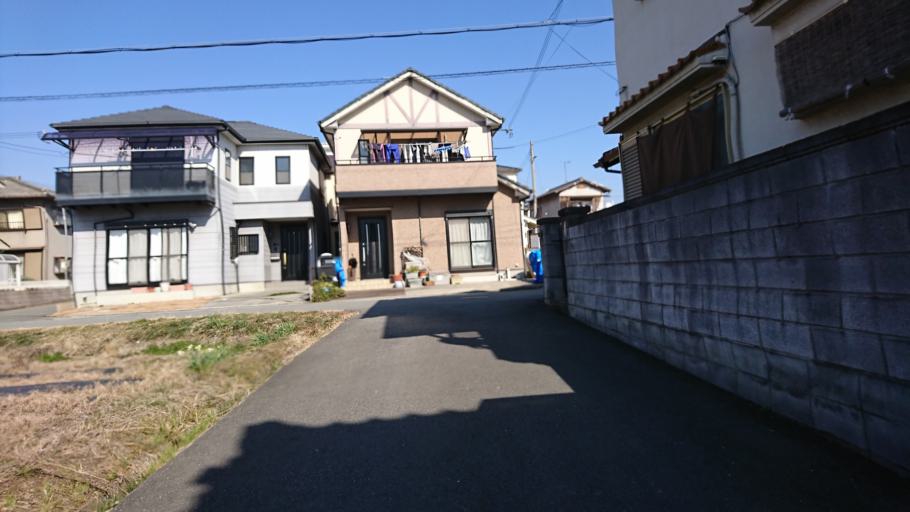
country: JP
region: Hyogo
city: Kakogawacho-honmachi
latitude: 34.7331
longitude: 134.8702
